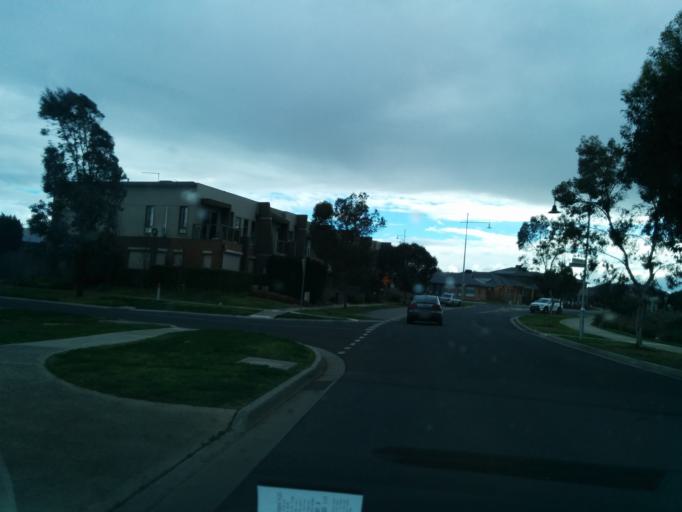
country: AU
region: Victoria
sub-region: Wyndham
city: Point Cook
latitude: -37.9080
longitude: 144.7274
